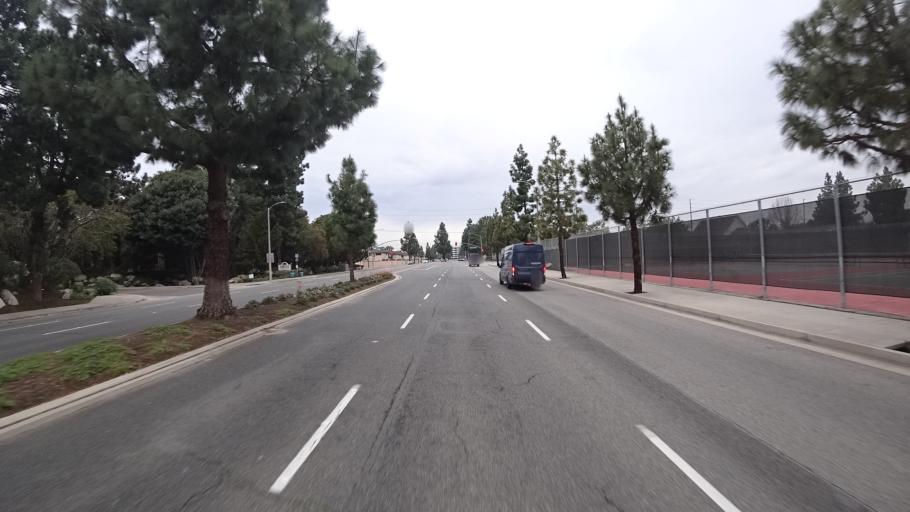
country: US
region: California
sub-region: Orange County
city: Fountain Valley
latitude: 33.7000
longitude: -117.9028
